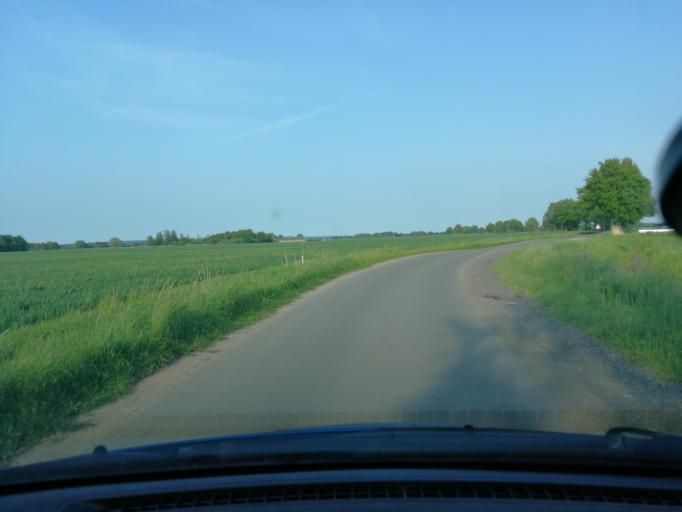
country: DE
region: Lower Saxony
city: Handorf
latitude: 53.3635
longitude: 10.3537
